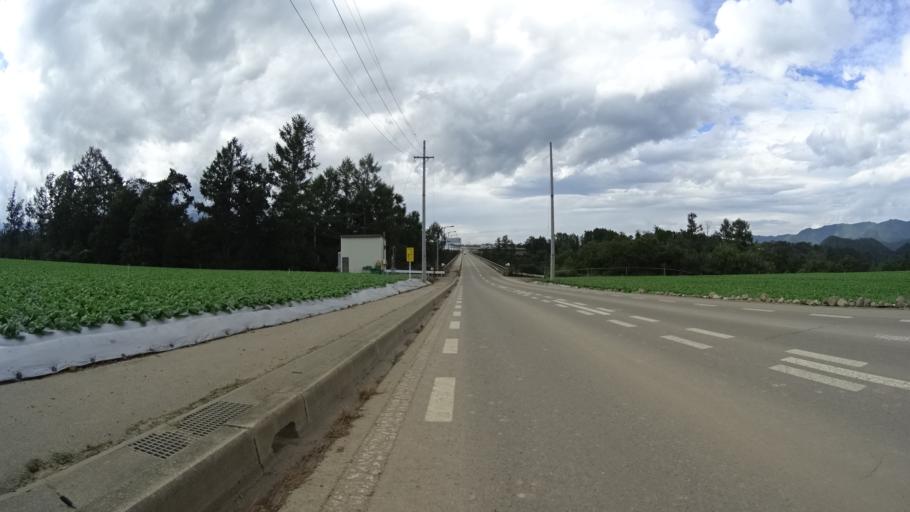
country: JP
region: Nagano
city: Saku
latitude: 35.9715
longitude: 138.5143
